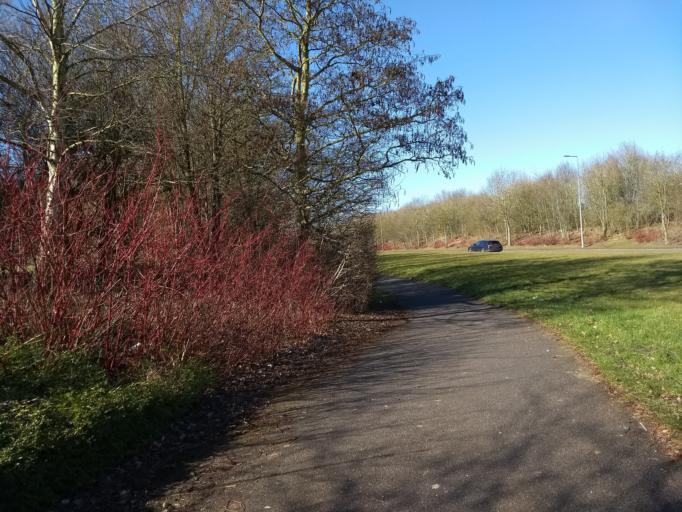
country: GB
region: England
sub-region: Milton Keynes
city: Shenley Church End
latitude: 52.0014
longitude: -0.7817
